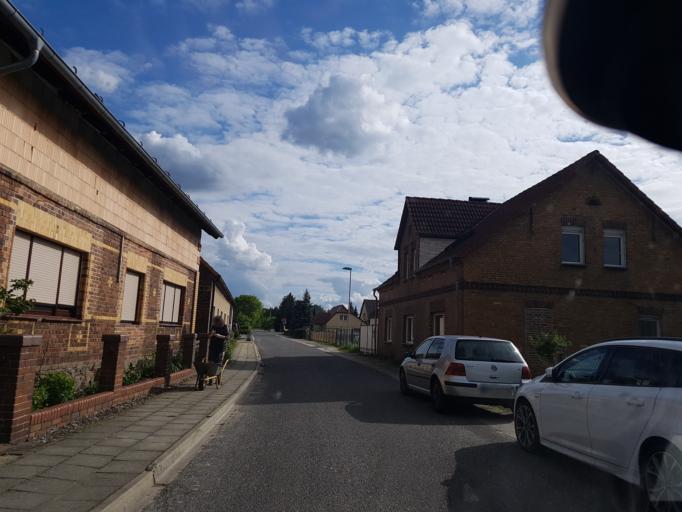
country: DE
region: Brandenburg
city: Sallgast
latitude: 51.6027
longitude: 13.9041
